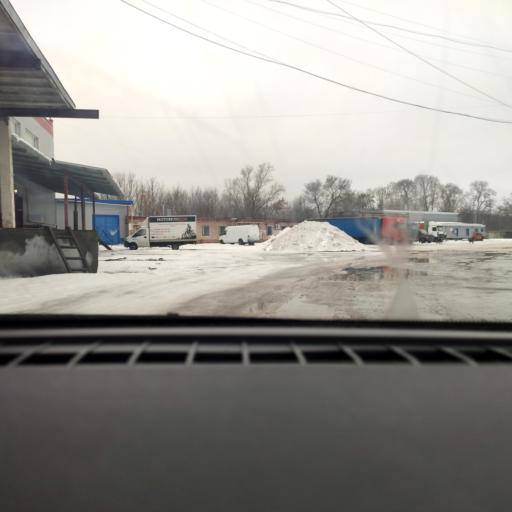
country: RU
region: Voronezj
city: Maslovka
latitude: 51.6367
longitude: 39.3020
